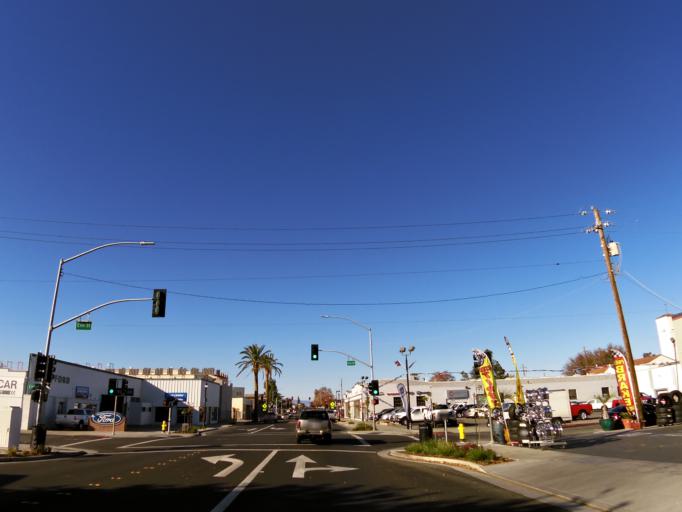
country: US
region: California
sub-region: Yolo County
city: Woodland
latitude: 38.6775
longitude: -121.7759
